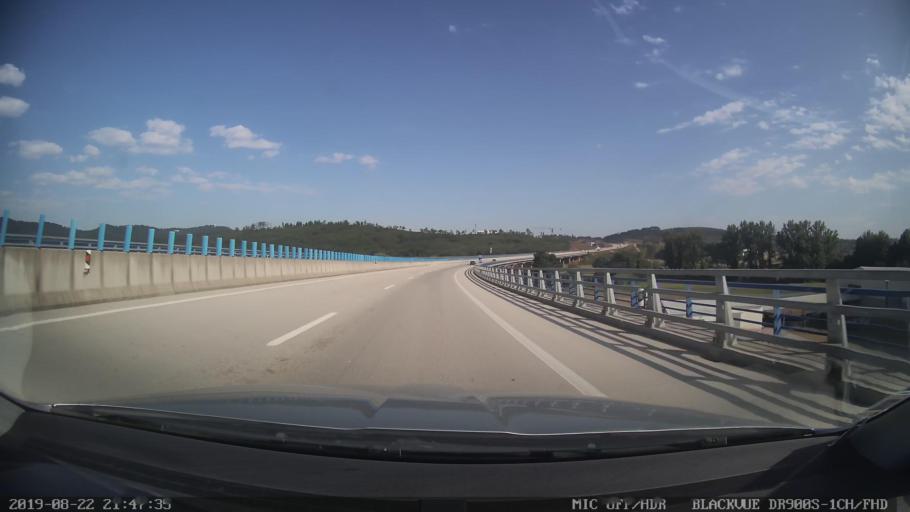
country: PT
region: Coimbra
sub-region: Penela
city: Penela
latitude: 40.0086
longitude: -8.3668
